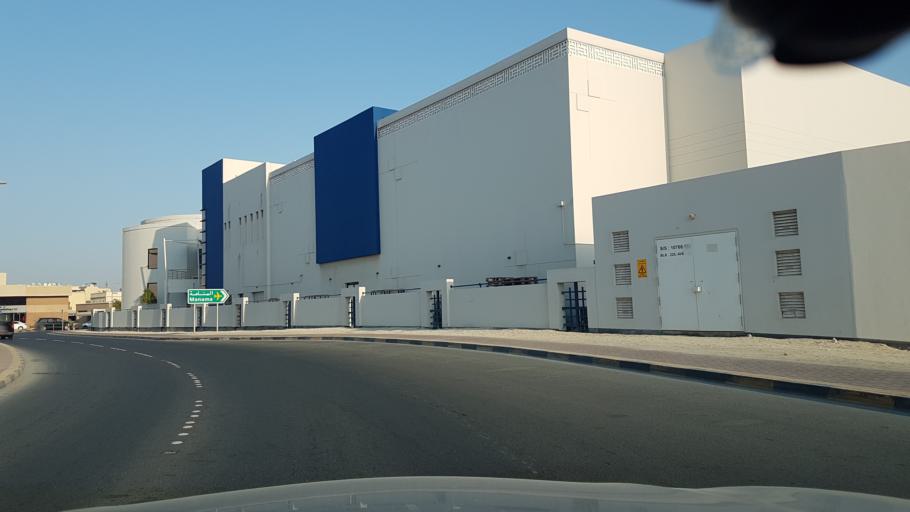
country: BH
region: Muharraq
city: Al Muharraq
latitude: 26.2716
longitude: 50.6030
